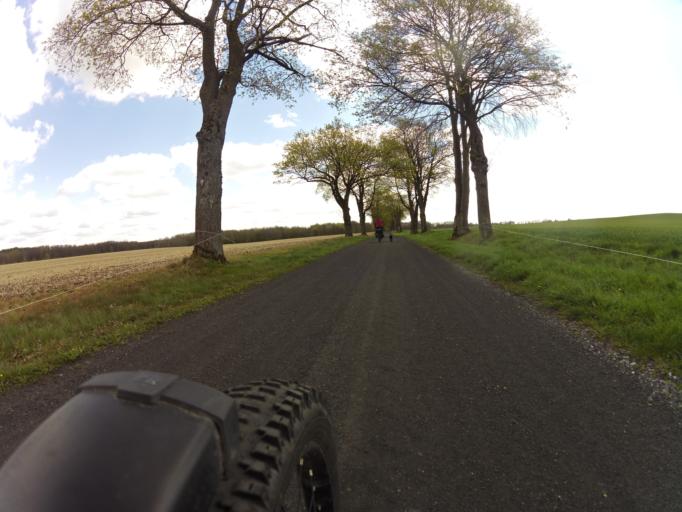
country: PL
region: West Pomeranian Voivodeship
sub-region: Powiat gryficki
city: Gryfice
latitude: 53.8519
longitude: 15.1696
